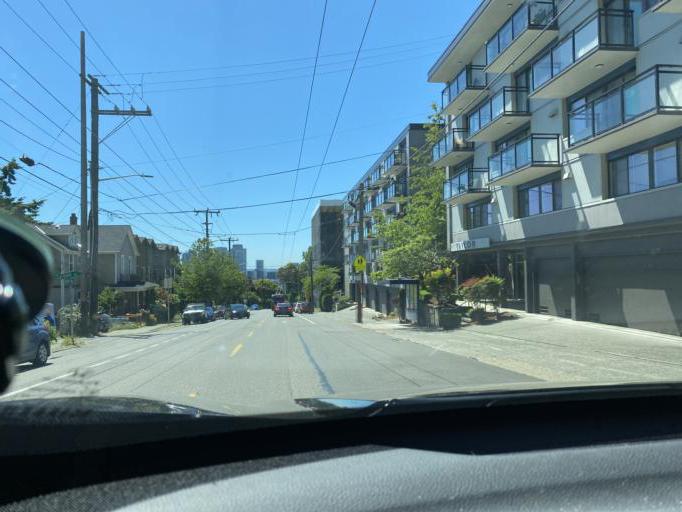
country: US
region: Washington
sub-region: King County
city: Seattle
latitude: 47.6335
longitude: -122.3460
